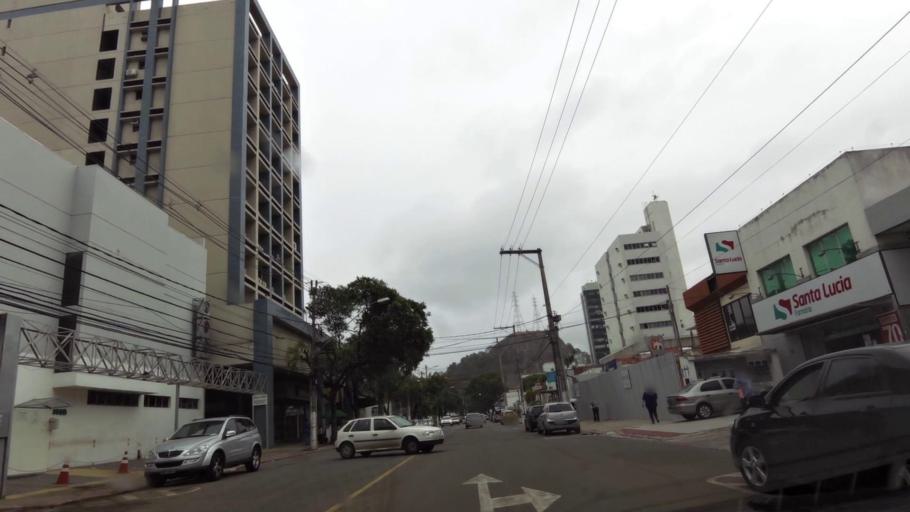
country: BR
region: Espirito Santo
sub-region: Vila Velha
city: Vila Velha
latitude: -20.3119
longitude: -40.3003
